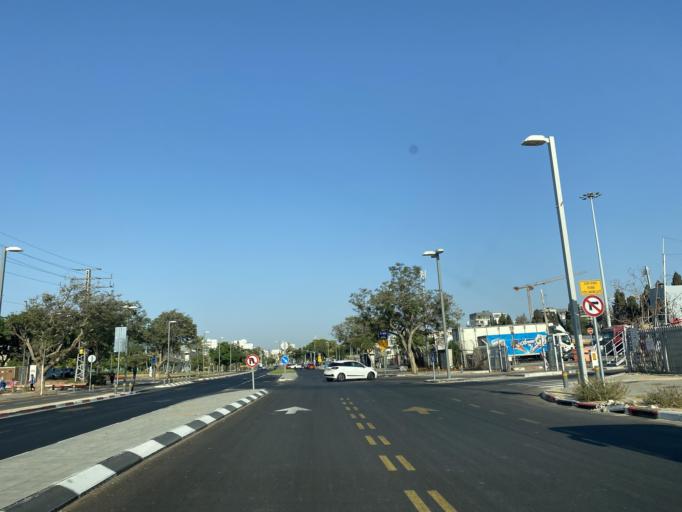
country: IL
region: Tel Aviv
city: Herzliyya
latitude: 32.1643
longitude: 34.8207
